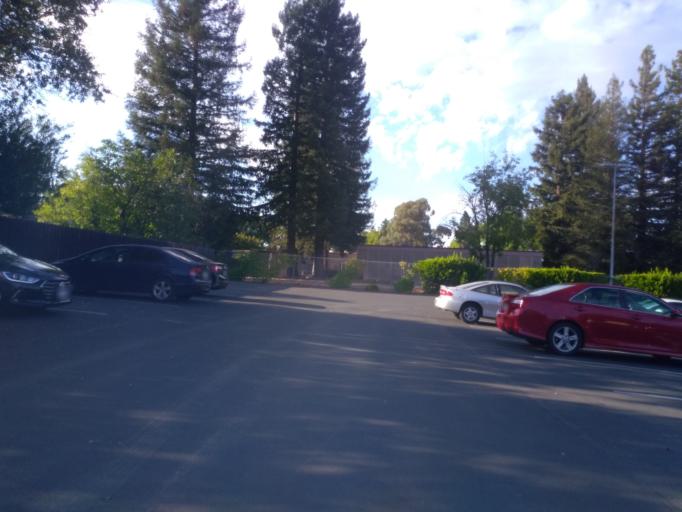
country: US
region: California
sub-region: Mendocino County
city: Ukiah
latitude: 39.1351
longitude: -123.2108
